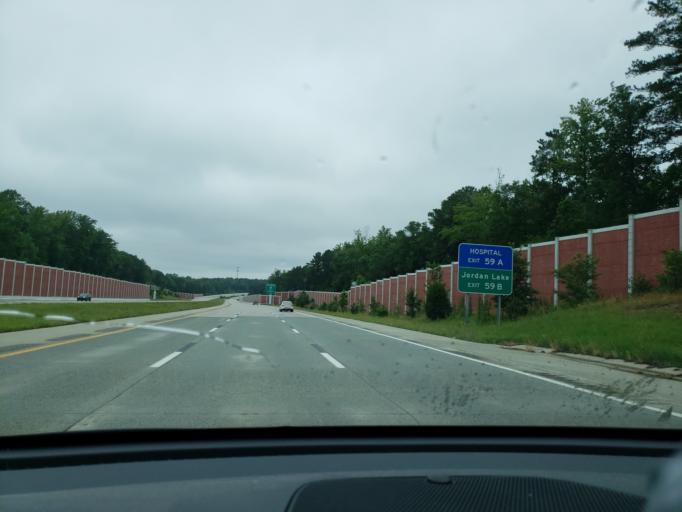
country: US
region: North Carolina
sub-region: Wake County
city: Apex
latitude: 35.7239
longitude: -78.8872
